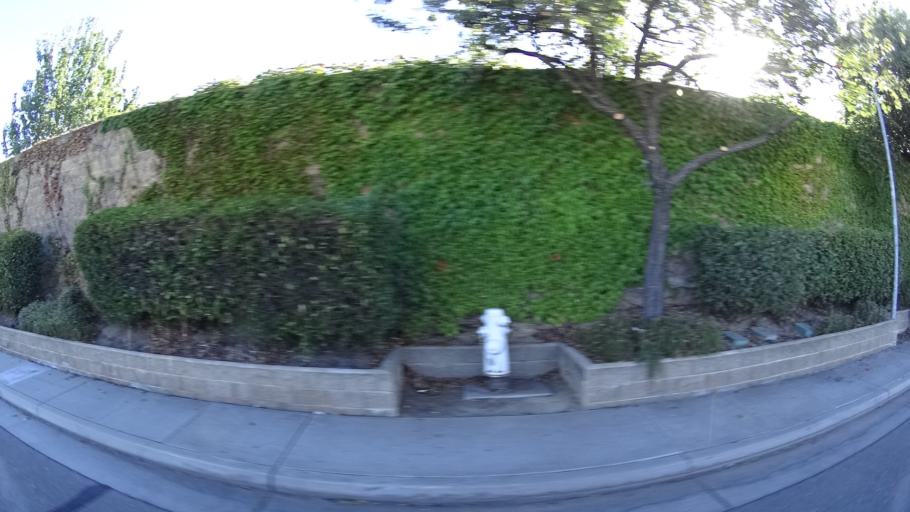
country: US
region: California
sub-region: Sacramento County
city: Laguna
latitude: 38.4498
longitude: -121.4067
